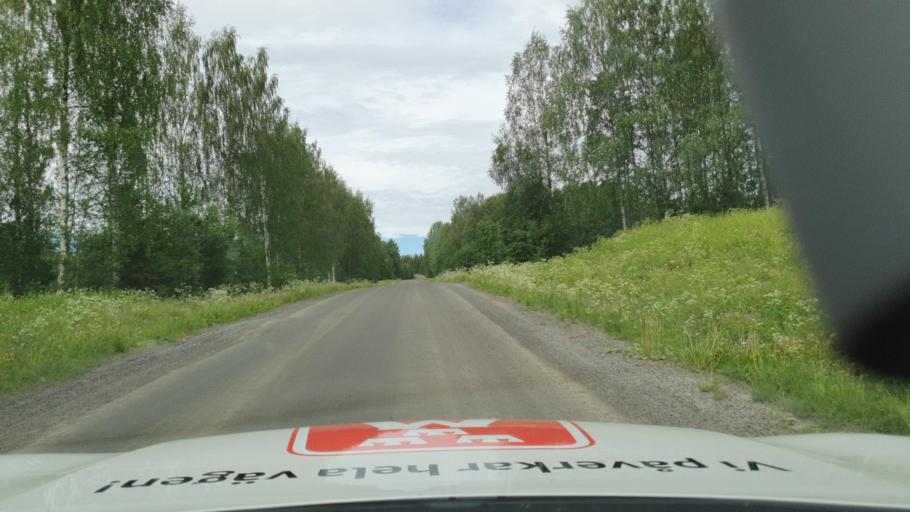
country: SE
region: Vaesterbotten
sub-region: Skelleftea Kommun
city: Burtraesk
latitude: 64.3625
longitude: 20.4104
